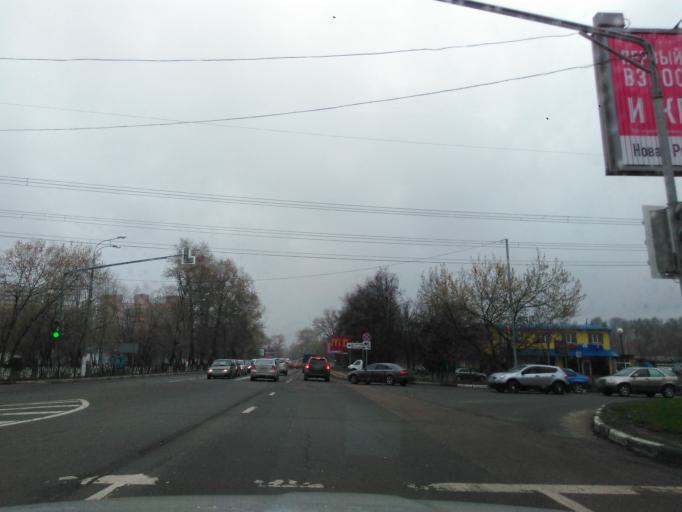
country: RU
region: Moskovskaya
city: Krasnogorsk
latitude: 55.8318
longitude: 37.3032
